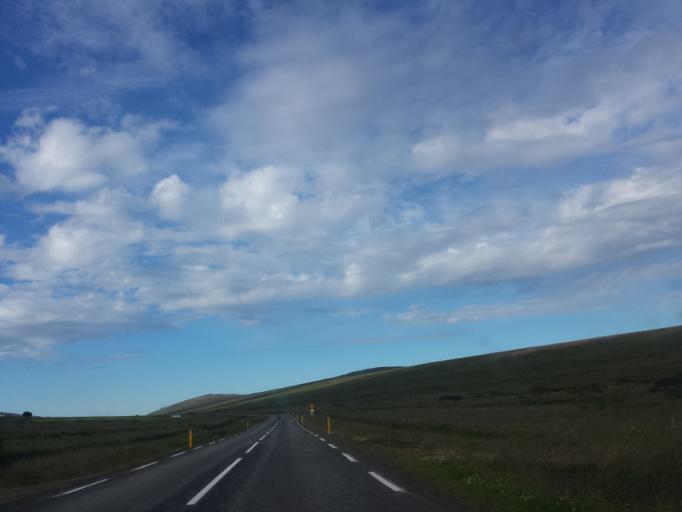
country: IS
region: Northeast
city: Laugar
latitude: 65.7263
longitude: -17.5948
